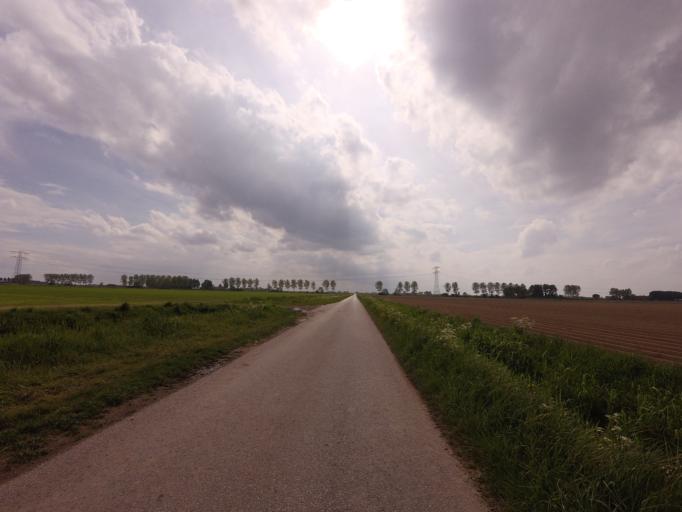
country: NL
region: South Holland
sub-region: Gemeente Goeree-Overflakkee
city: Middelharnis
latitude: 51.7282
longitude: 4.2361
